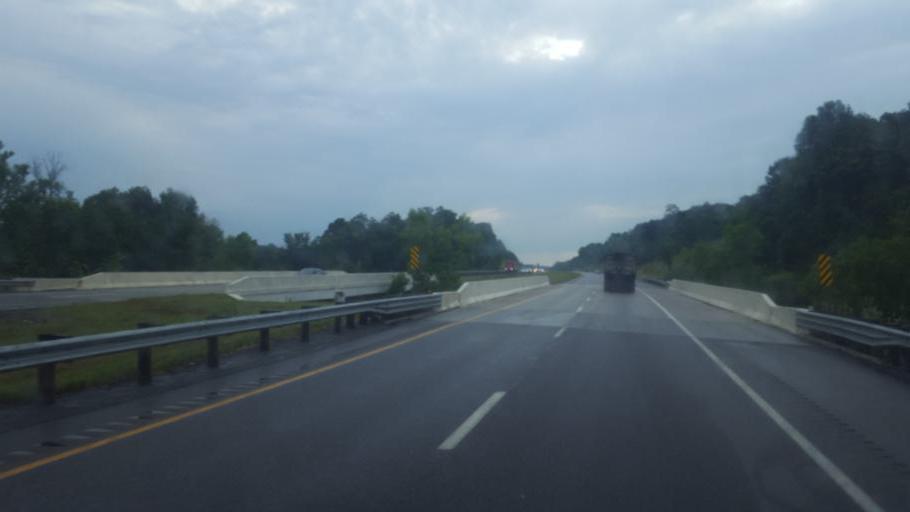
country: US
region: Ohio
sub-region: Geauga County
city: Bainbridge
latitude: 41.3877
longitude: -81.3813
